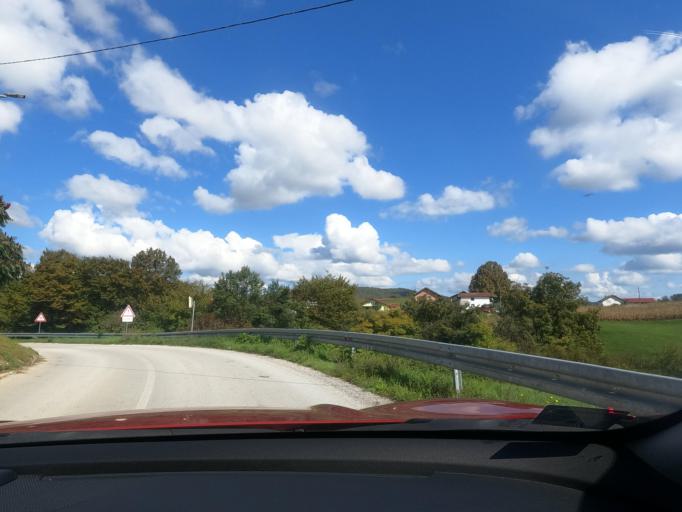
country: BA
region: Federation of Bosnia and Herzegovina
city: Velika Kladusa
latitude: 45.2057
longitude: 15.8078
